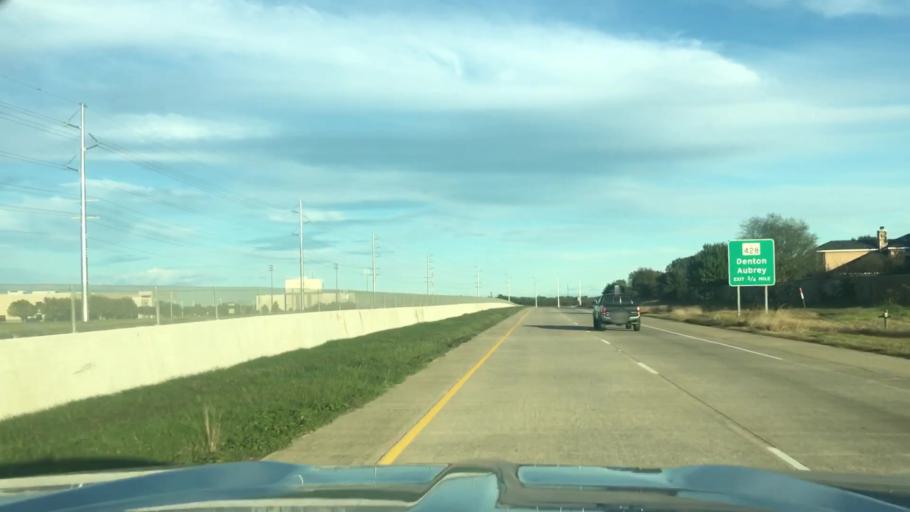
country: US
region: Texas
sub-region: Denton County
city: Denton
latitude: 33.2601
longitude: -97.1216
